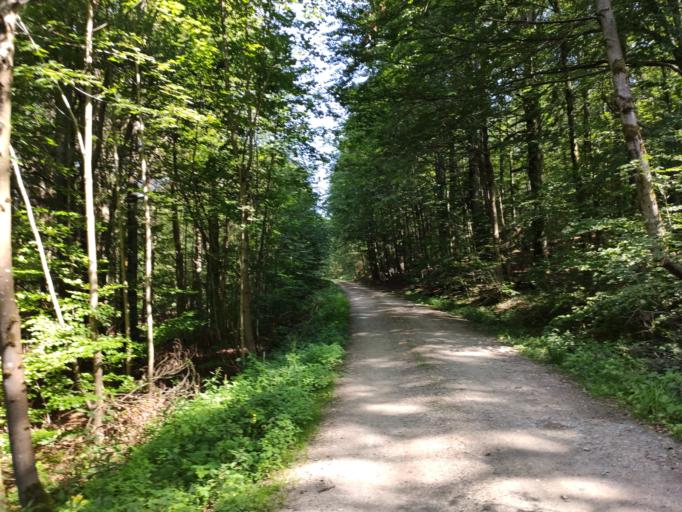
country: DE
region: Bavaria
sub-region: Upper Franconia
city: Nordhalben
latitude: 50.4006
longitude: 11.5485
